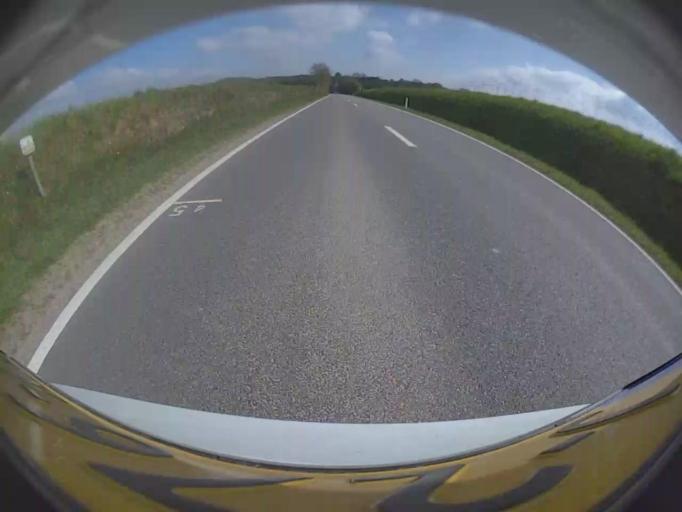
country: BE
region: Wallonia
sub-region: Province du Luxembourg
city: Tellin
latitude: 50.1080
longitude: 5.2361
